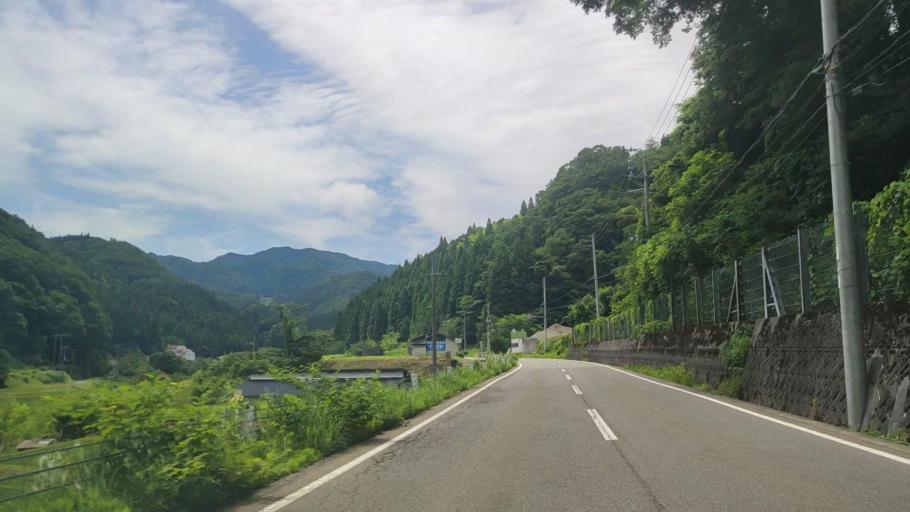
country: JP
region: Hyogo
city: Toyooka
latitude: 35.4773
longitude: 134.5522
